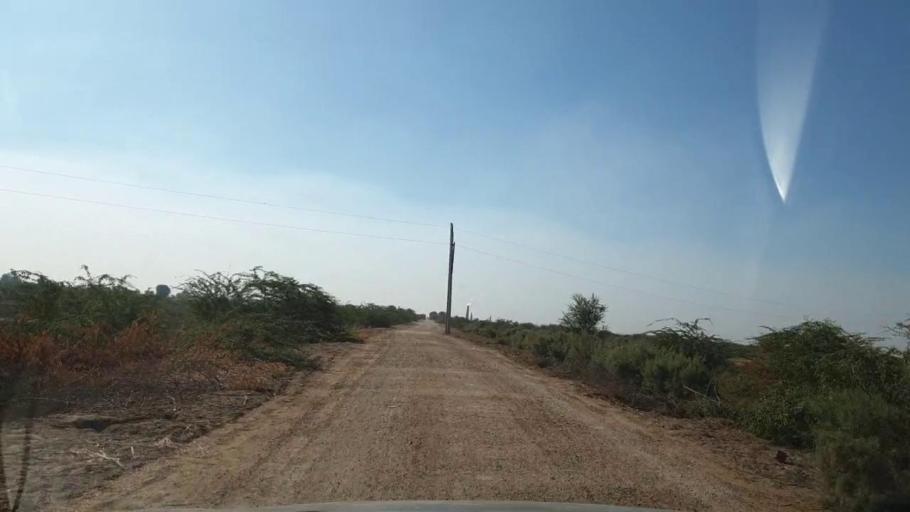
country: PK
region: Sindh
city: Jhol
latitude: 25.8093
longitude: 69.0098
